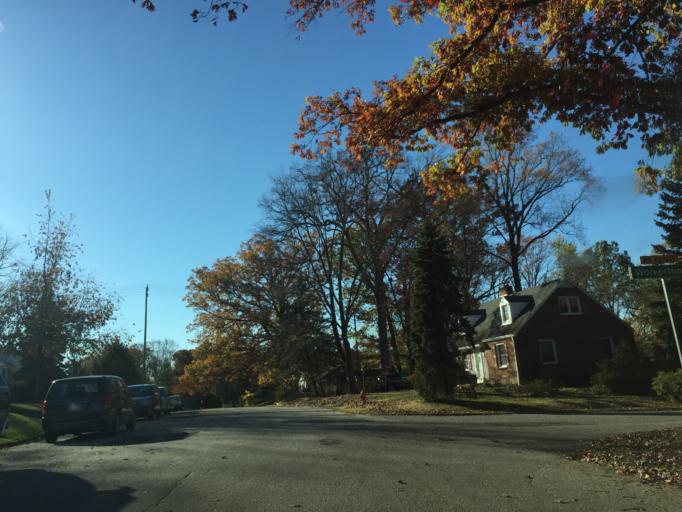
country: US
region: Maryland
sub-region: Baltimore County
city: Parkville
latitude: 39.4035
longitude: -76.5547
